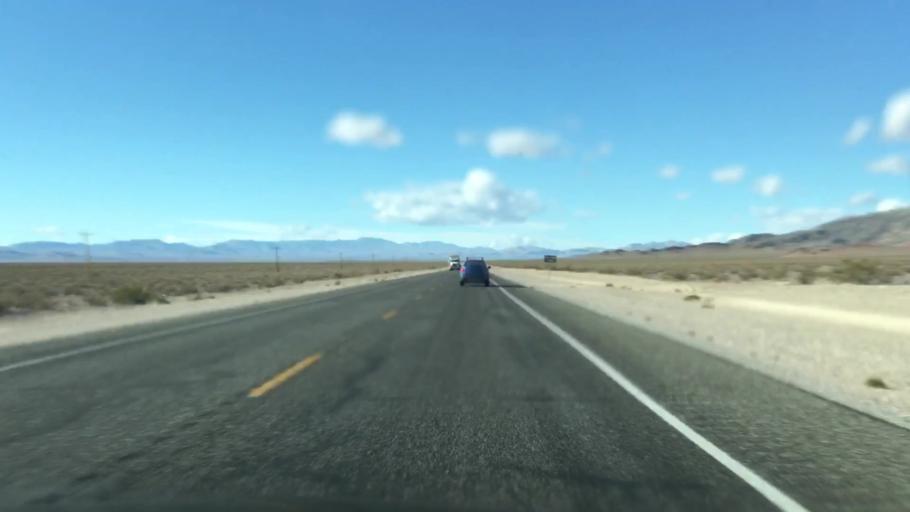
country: US
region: Nevada
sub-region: Nye County
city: Beatty
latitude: 36.7100
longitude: -116.5981
